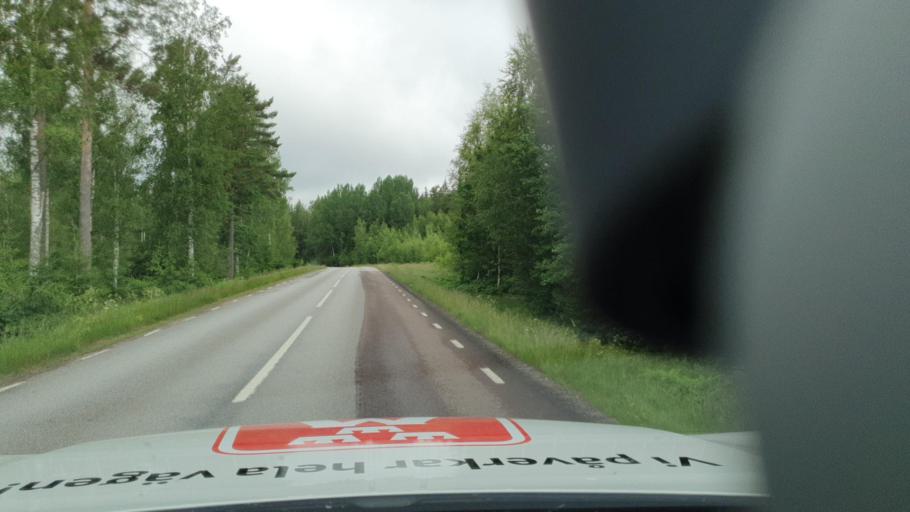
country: SE
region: Vaermland
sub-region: Kristinehamns Kommun
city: Bjorneborg
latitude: 59.0986
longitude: 14.2605
